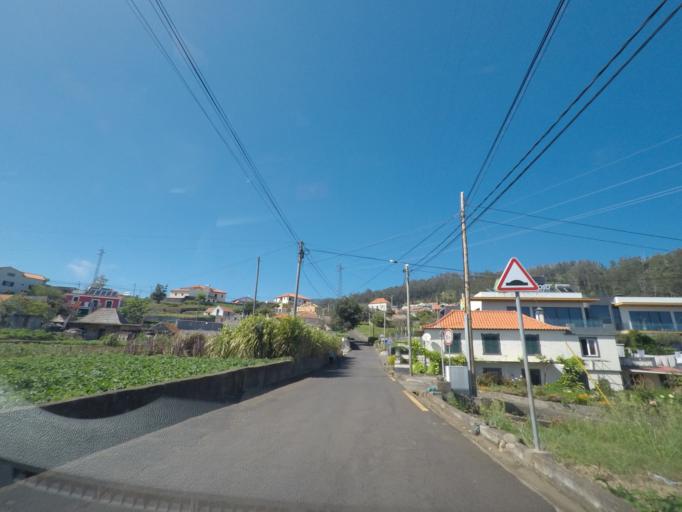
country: PT
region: Madeira
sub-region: Calheta
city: Arco da Calheta
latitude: 32.7072
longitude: -17.1165
